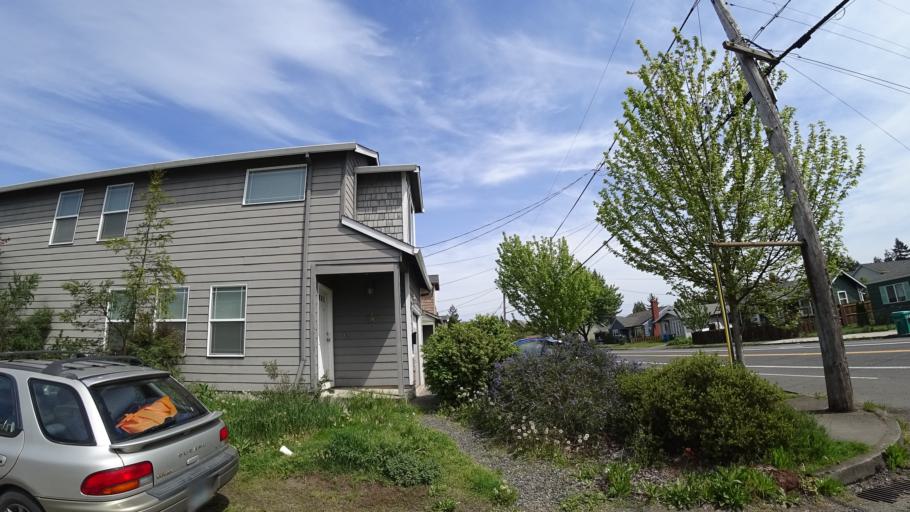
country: US
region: Oregon
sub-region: Clackamas County
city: Milwaukie
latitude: 45.4688
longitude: -122.6073
